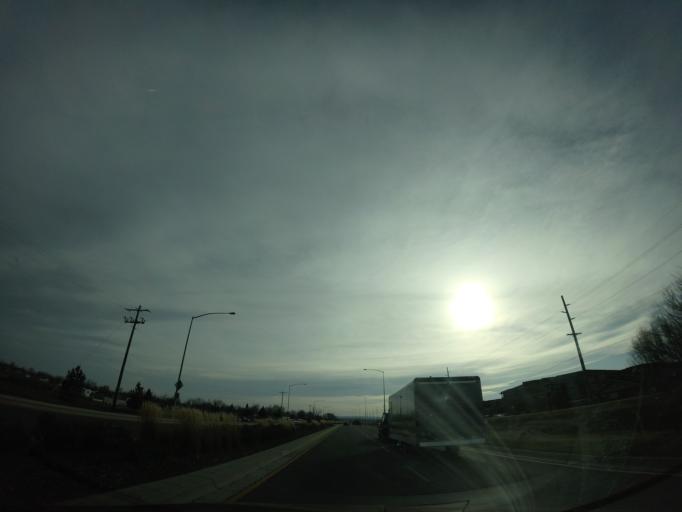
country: US
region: Montana
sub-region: Yellowstone County
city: Billings
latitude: 45.7684
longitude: -108.6177
